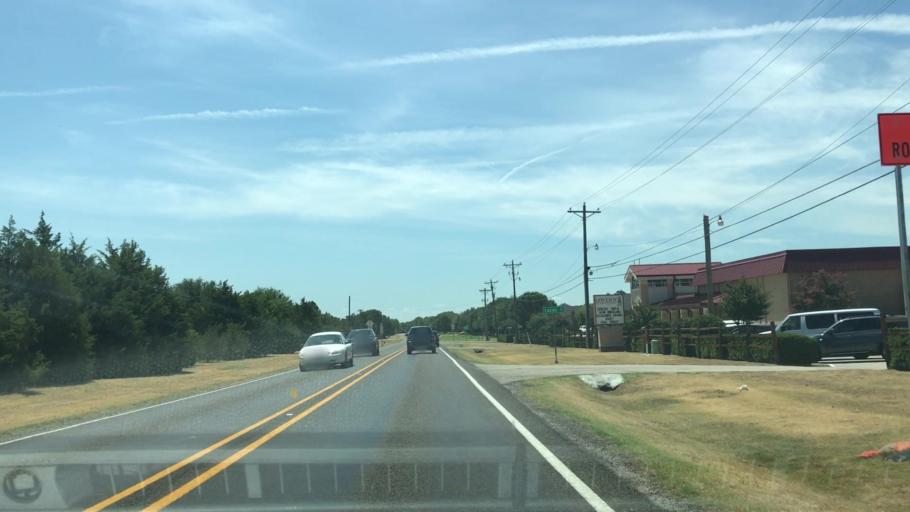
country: US
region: Texas
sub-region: Collin County
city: Fairview
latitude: 33.1264
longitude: -96.6108
